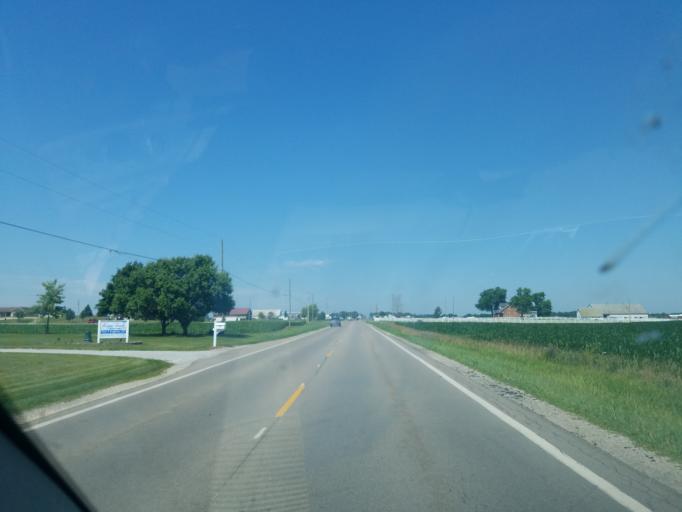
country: US
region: Ohio
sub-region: Auglaize County
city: Minster
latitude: 40.4076
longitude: -84.4529
